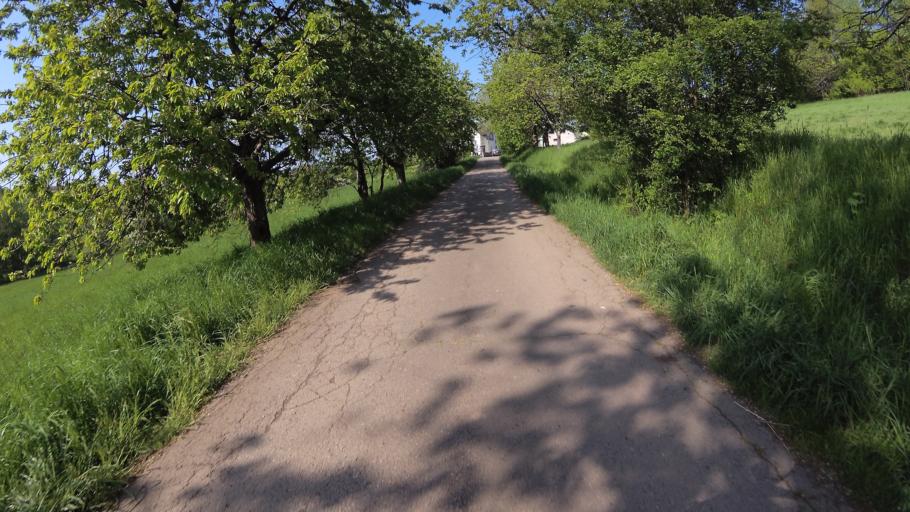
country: DE
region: Saarland
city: Merchweiler
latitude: 49.3560
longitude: 7.0458
